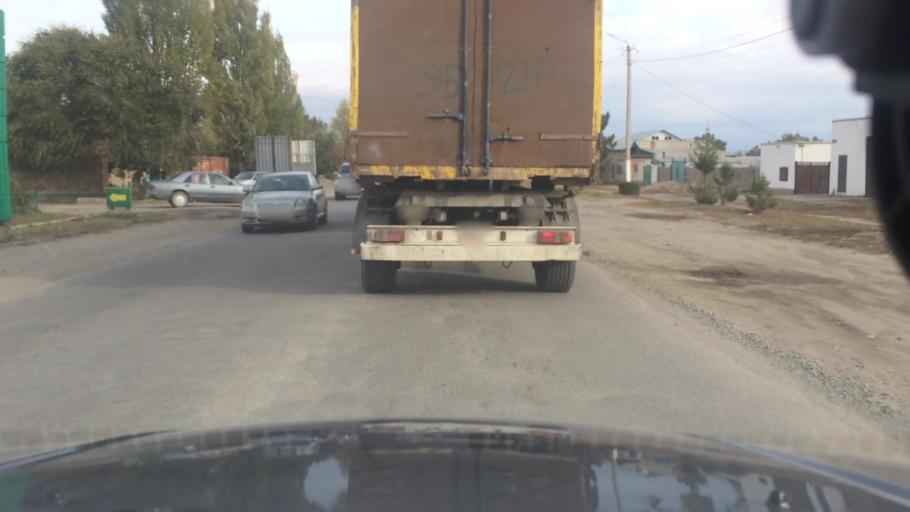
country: KG
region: Ysyk-Koel
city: Karakol
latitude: 42.5179
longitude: 78.3858
